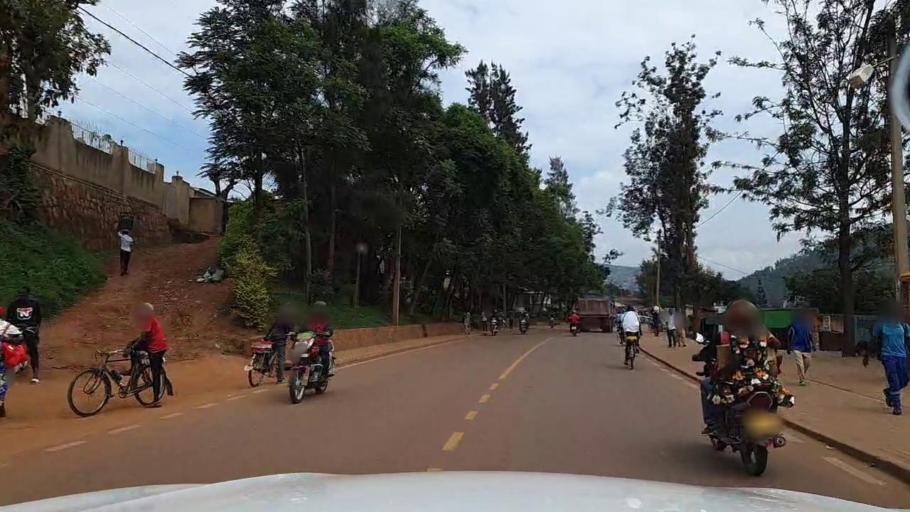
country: RW
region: Kigali
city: Kigali
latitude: -1.9246
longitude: 30.0462
